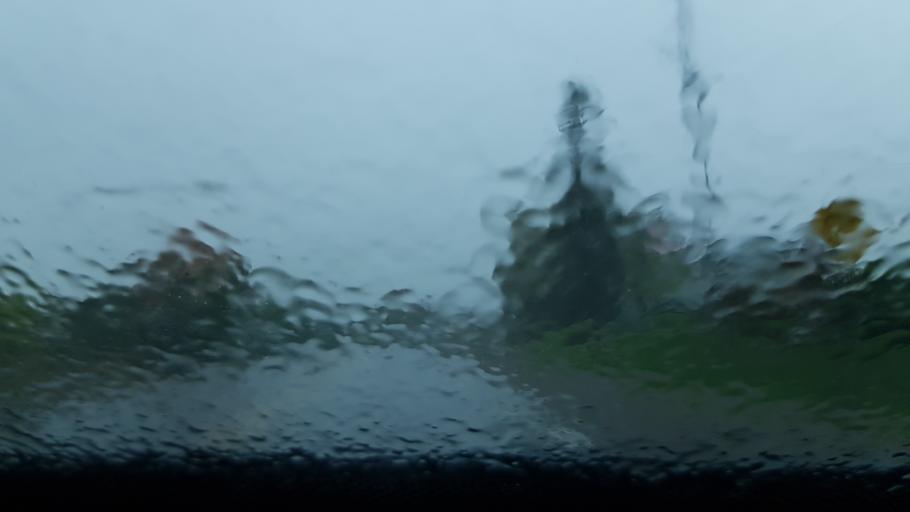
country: CA
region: Ontario
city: Omemee
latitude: 44.3458
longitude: -78.5446
